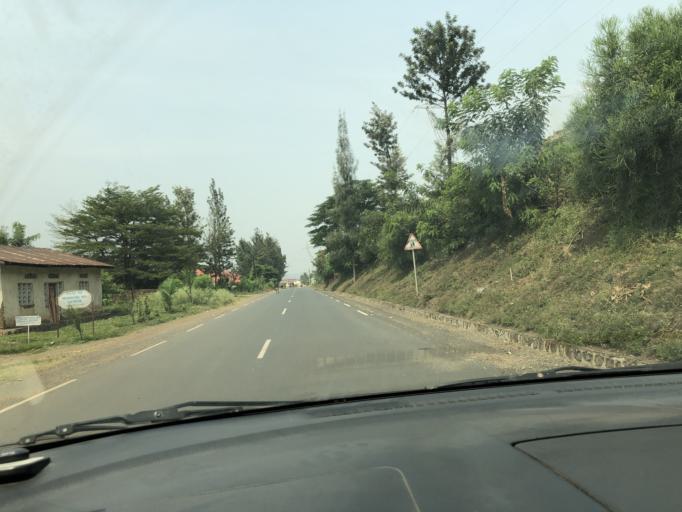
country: BI
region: Cibitoke
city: Cibitoke
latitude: -2.6962
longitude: 29.0040
